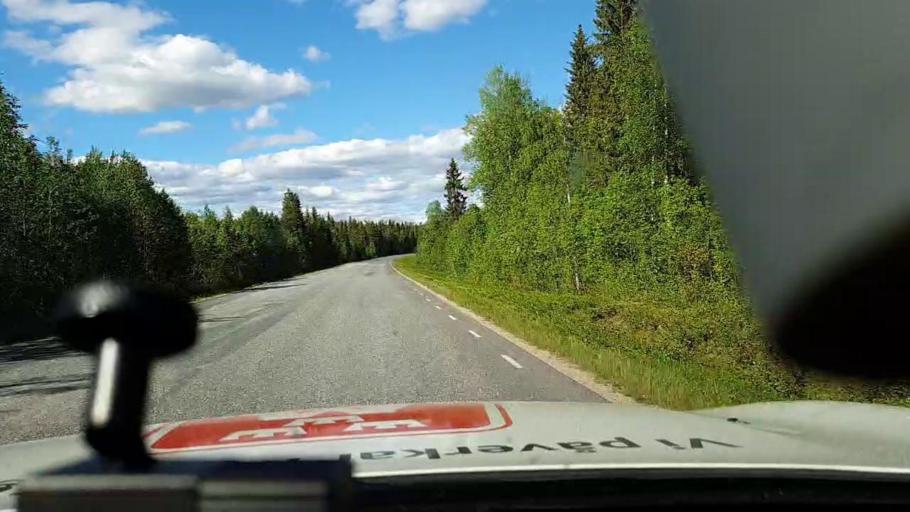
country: FI
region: Lapland
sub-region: Torniolaakso
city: Ylitornio
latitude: 66.3215
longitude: 23.6215
